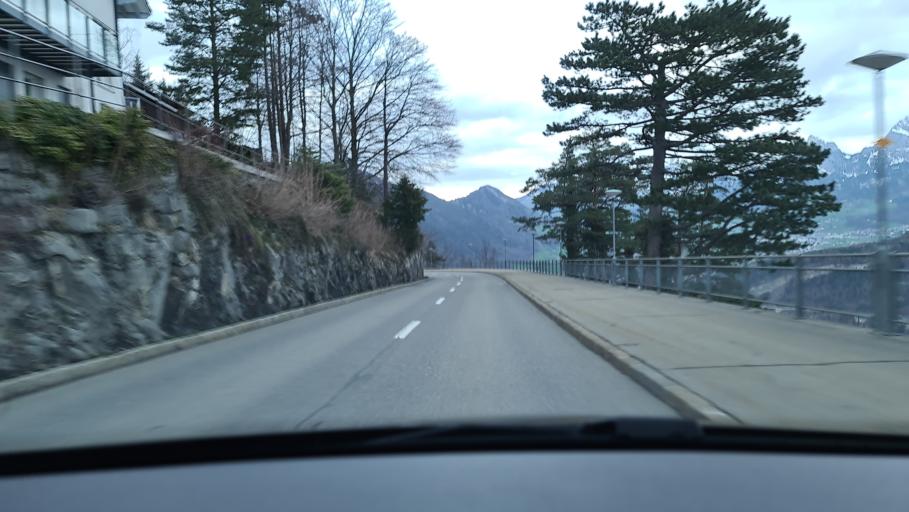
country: CH
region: Uri
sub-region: Uri
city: Bauen
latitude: 46.9718
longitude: 8.5873
